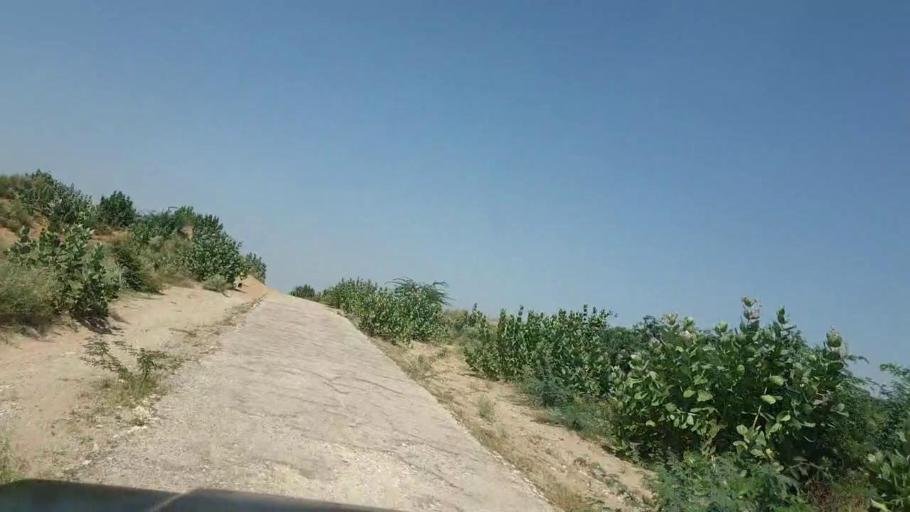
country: PK
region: Sindh
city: Chor
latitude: 25.3983
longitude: 70.3124
